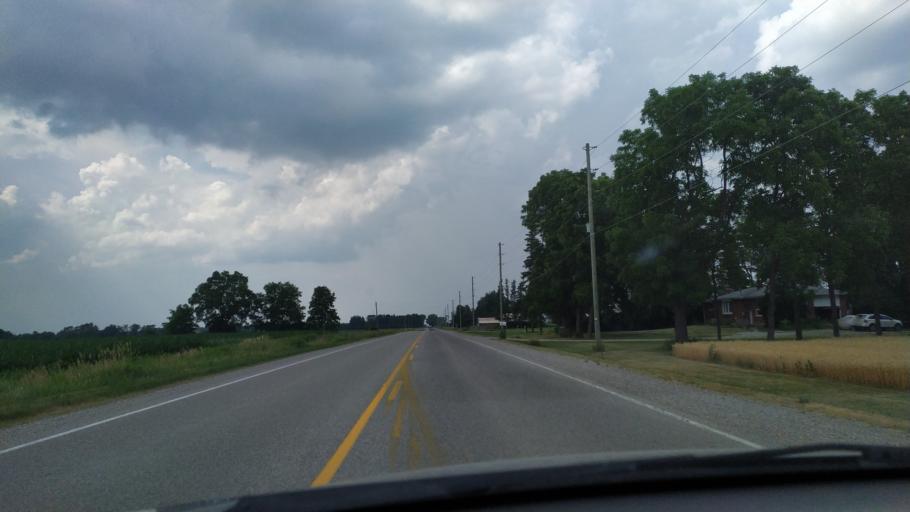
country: CA
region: Ontario
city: London
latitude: 43.1444
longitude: -81.1787
